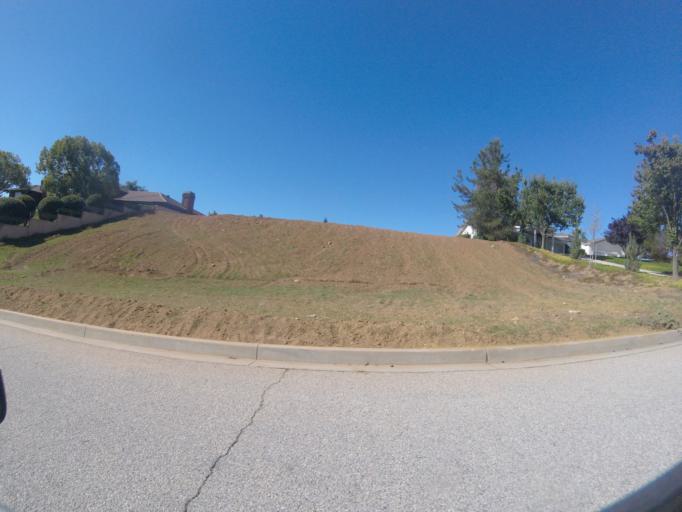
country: US
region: California
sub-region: San Bernardino County
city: Mentone
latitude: 34.0189
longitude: -117.1236
